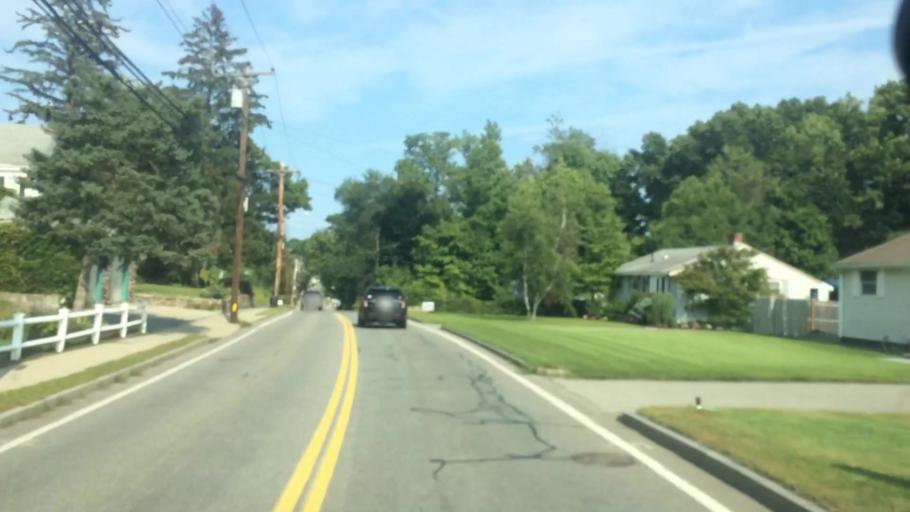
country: US
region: Massachusetts
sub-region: Middlesex County
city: Woburn
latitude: 42.4804
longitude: -71.1802
